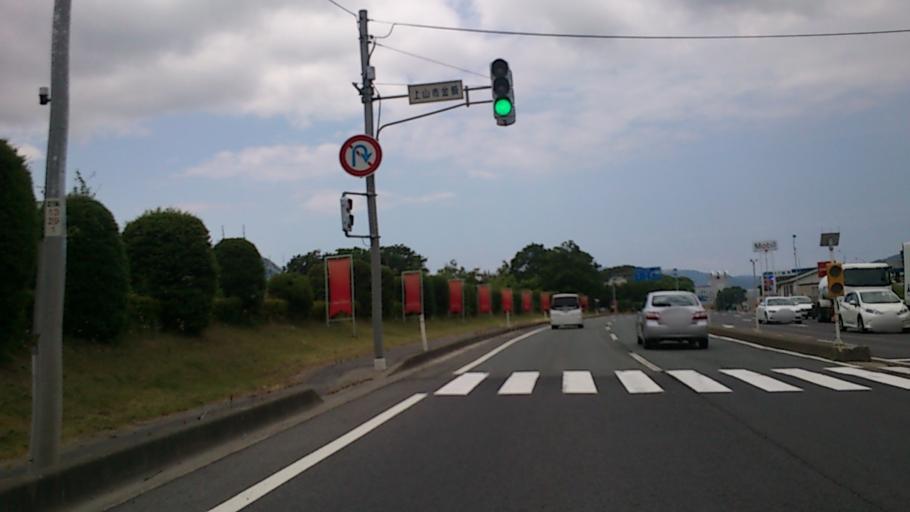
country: JP
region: Yamagata
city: Kaminoyama
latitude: 38.1790
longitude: 140.3094
